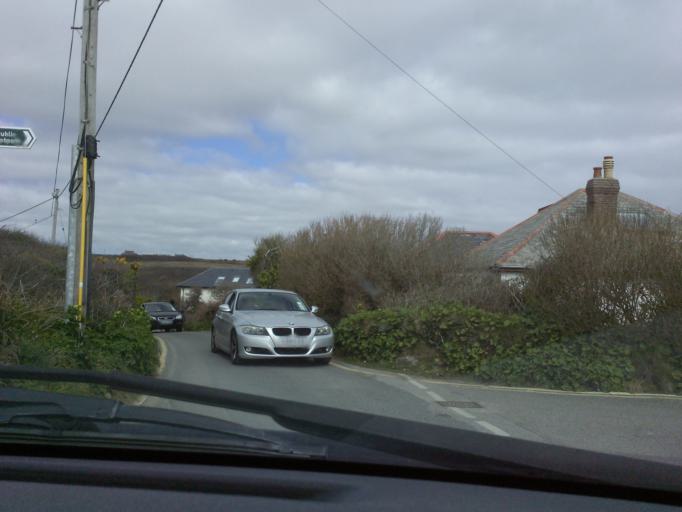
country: GB
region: England
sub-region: Cornwall
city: St. Buryan
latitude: 50.0429
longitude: -5.6544
